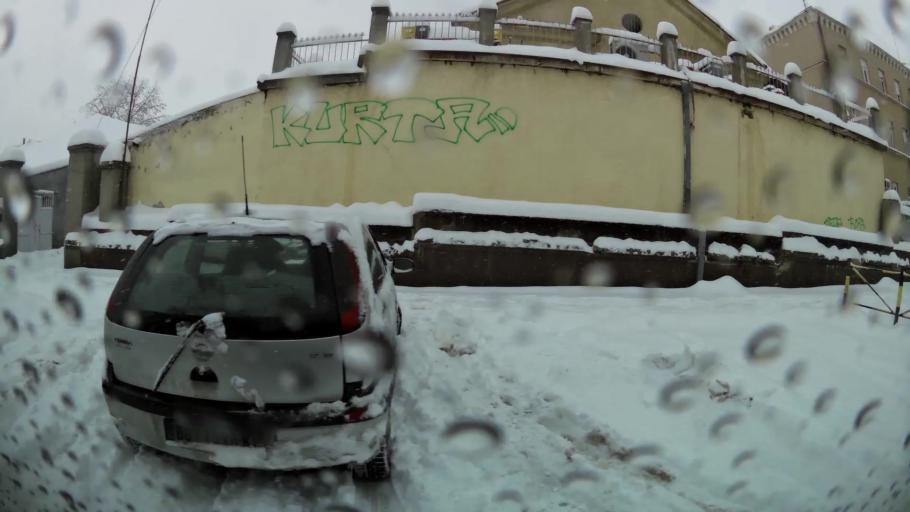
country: RS
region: Central Serbia
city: Belgrade
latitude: 44.7984
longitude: 20.4611
